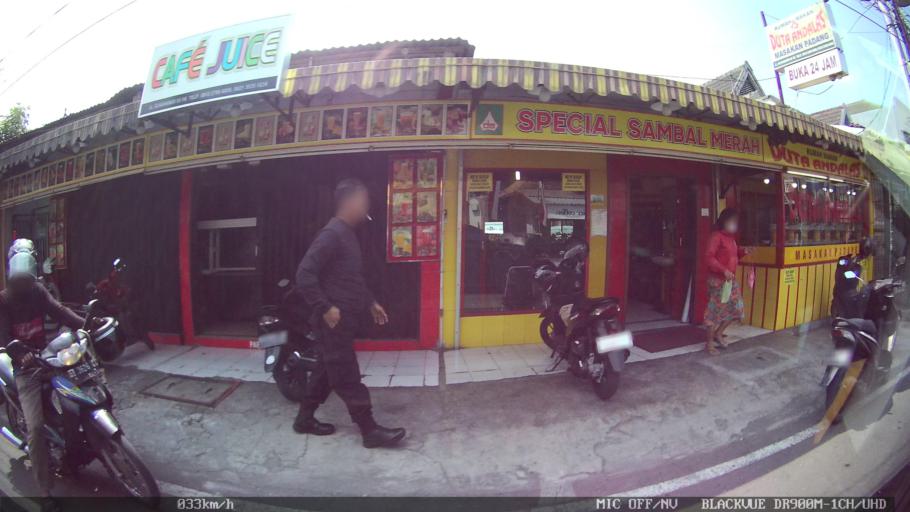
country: ID
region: Daerah Istimewa Yogyakarta
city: Yogyakarta
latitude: -7.8079
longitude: 110.3878
